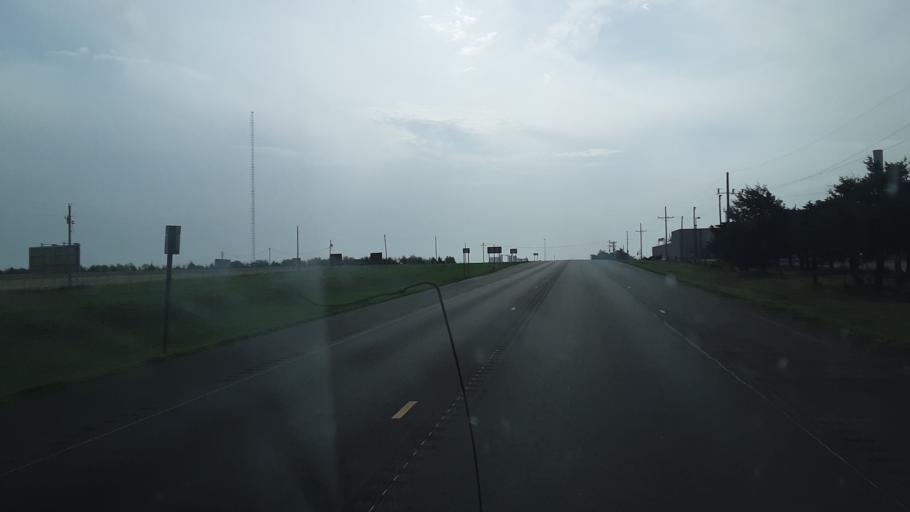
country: US
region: Kansas
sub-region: Ford County
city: Dodge City
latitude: 37.7792
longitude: -99.9334
